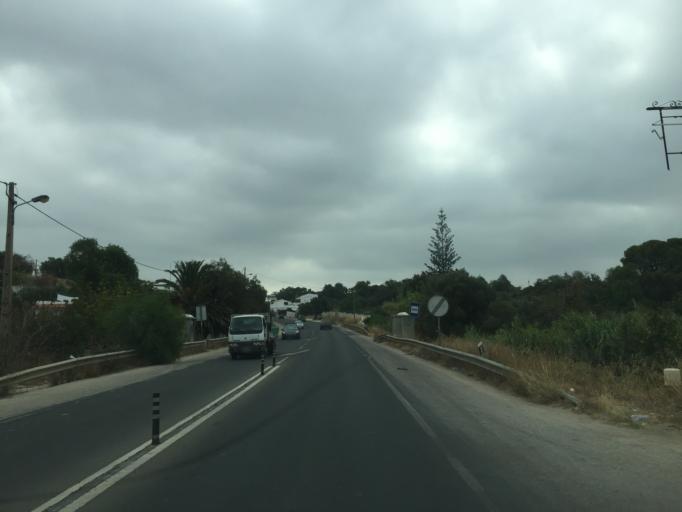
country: PT
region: Faro
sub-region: Loule
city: Almancil
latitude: 37.0813
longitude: -8.0081
